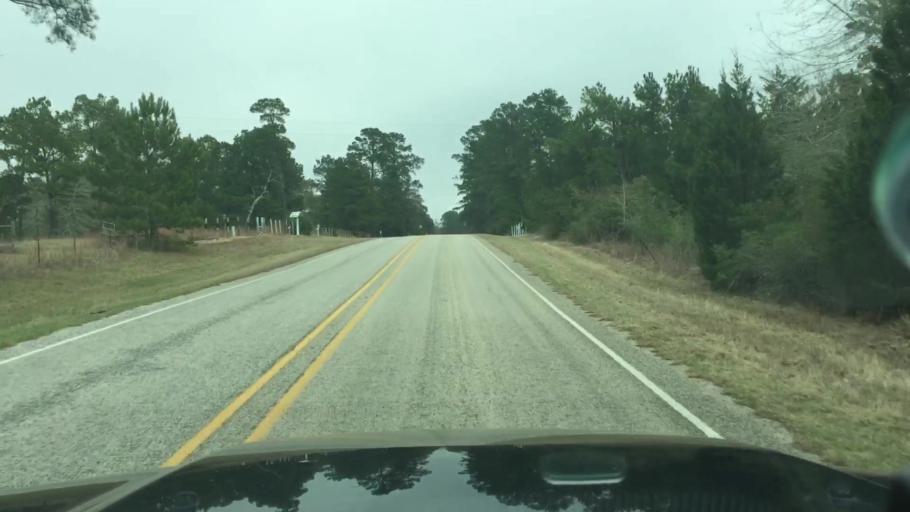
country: US
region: Texas
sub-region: Fayette County
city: La Grange
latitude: 30.0104
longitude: -96.9401
